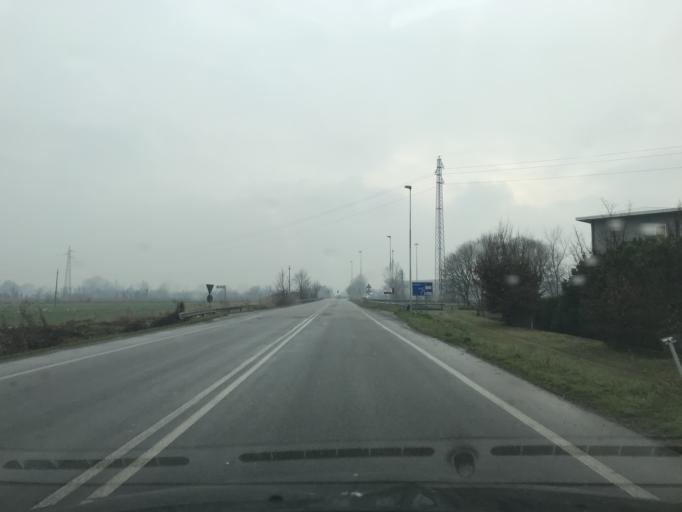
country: IT
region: Lombardy
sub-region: Provincia di Lodi
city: Massalengo-Motta Vigana
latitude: 45.2692
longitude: 9.5027
